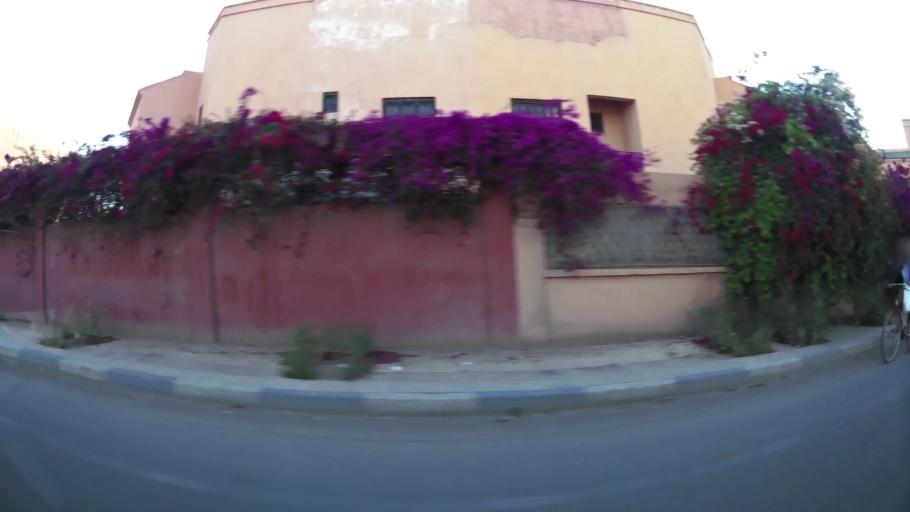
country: MA
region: Marrakech-Tensift-Al Haouz
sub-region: Marrakech
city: Marrakesh
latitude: 31.6720
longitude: -8.0586
